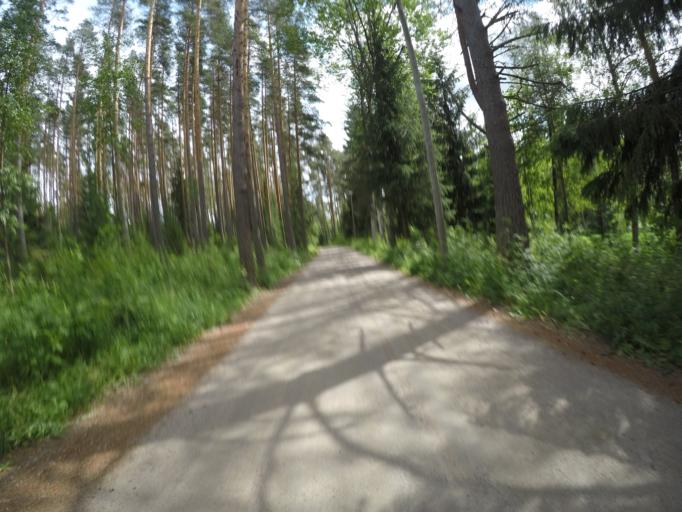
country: FI
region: Haeme
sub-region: Haemeenlinna
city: Haemeenlinna
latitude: 60.9721
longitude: 24.4253
